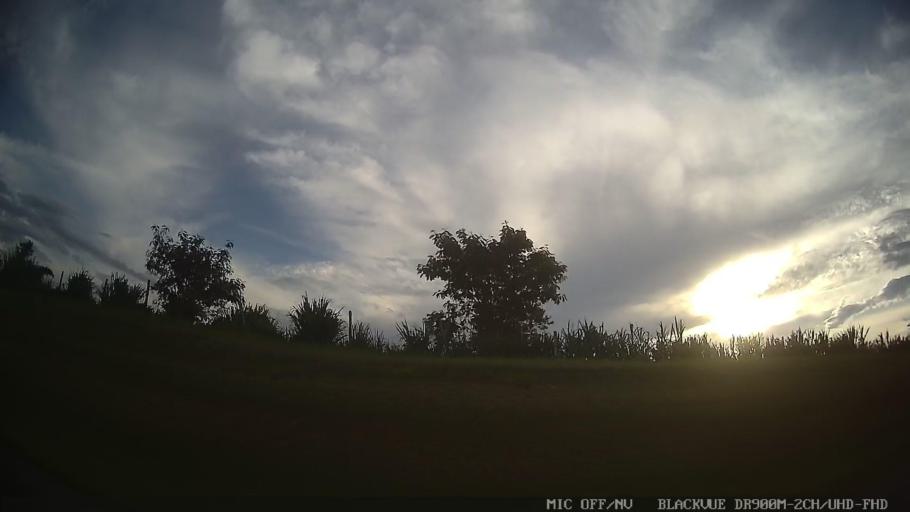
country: BR
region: Sao Paulo
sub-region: Porto Feliz
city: Porto Feliz
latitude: -23.2005
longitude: -47.6062
